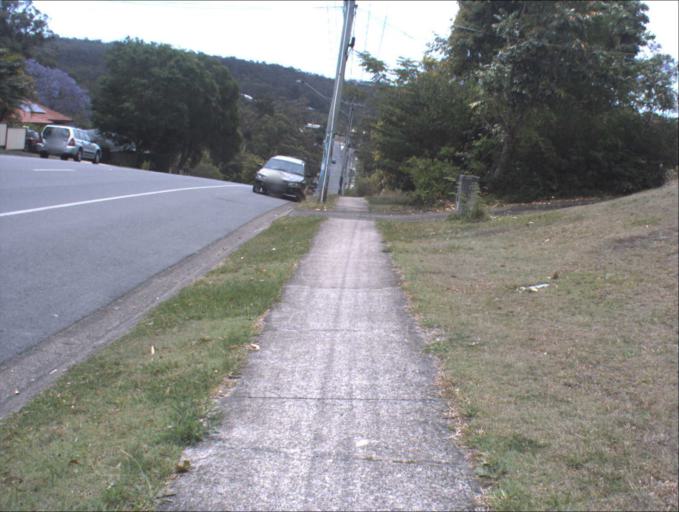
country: AU
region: Queensland
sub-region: Logan
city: Slacks Creek
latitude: -27.6477
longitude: 153.1737
